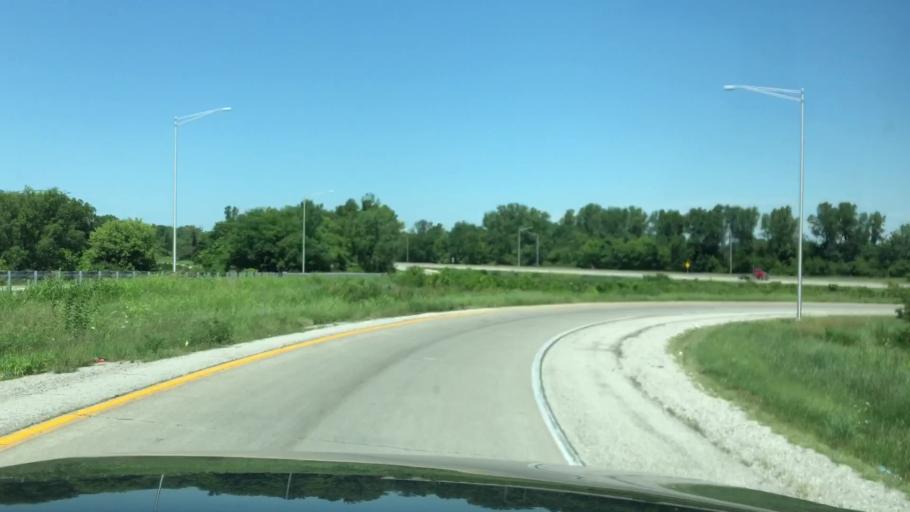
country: US
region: Illinois
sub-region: Saint Clair County
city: Alorton
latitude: 38.5824
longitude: -90.1107
